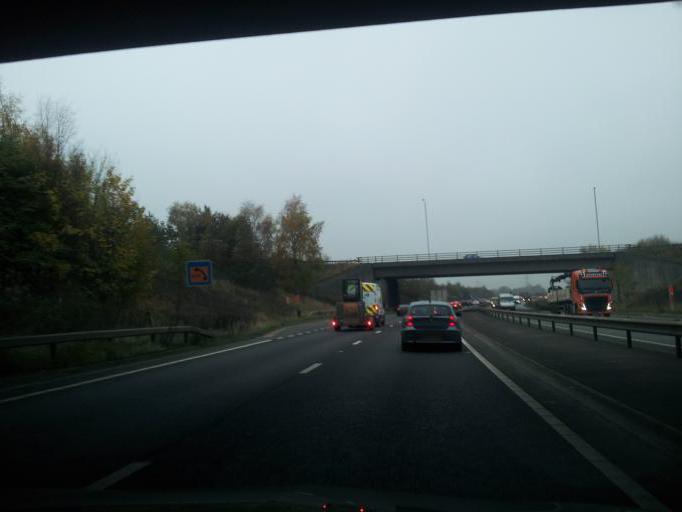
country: GB
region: England
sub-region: Leicestershire
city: Anstey
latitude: 52.6660
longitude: -1.1832
